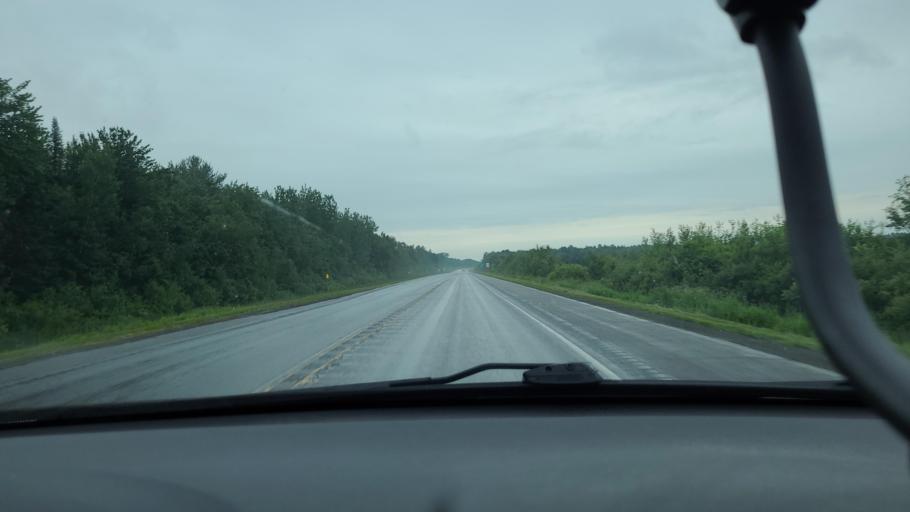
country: CA
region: Quebec
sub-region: Laurentides
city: Saint-Colomban
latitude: 45.6590
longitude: -74.2152
